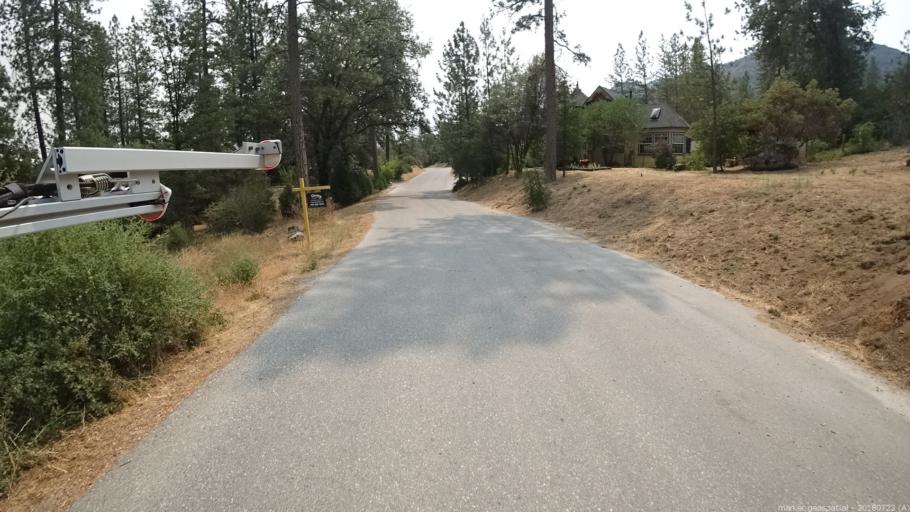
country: US
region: California
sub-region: Madera County
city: Ahwahnee
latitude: 37.3328
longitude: -119.7114
